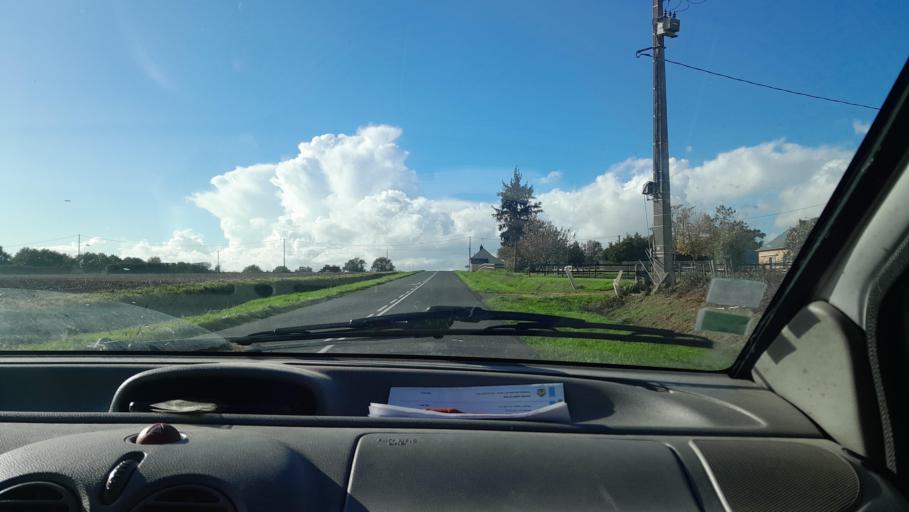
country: FR
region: Pays de la Loire
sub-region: Departement de la Mayenne
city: Cosse-le-Vivien
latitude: 47.9559
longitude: -0.9492
